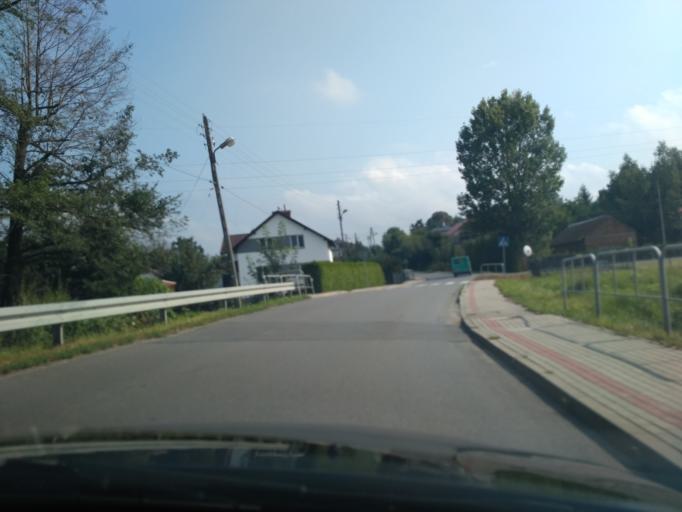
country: PL
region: Subcarpathian Voivodeship
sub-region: Powiat rzeszowski
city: Niechobrz
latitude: 50.0031
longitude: 21.8921
